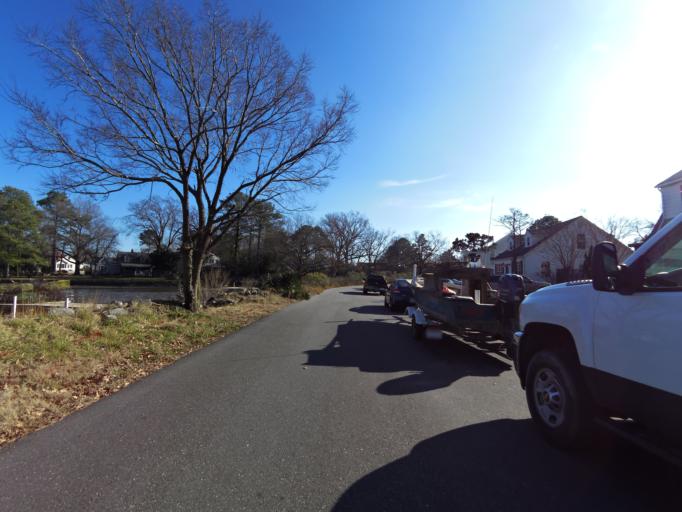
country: US
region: Virginia
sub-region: City of Hampton
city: Hampton
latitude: 37.0016
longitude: -76.3733
